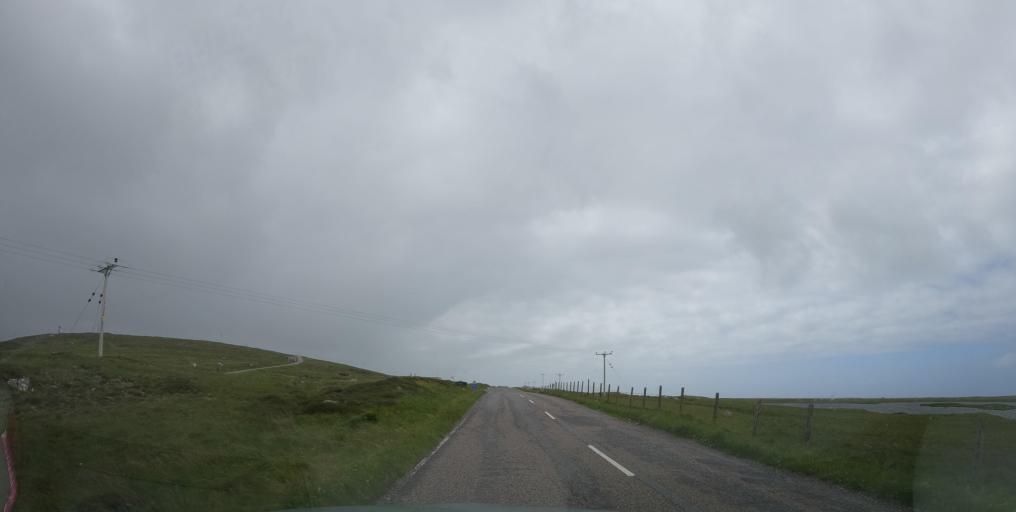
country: GB
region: Scotland
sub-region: Eilean Siar
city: Benbecula
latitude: 57.3484
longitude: -7.3593
